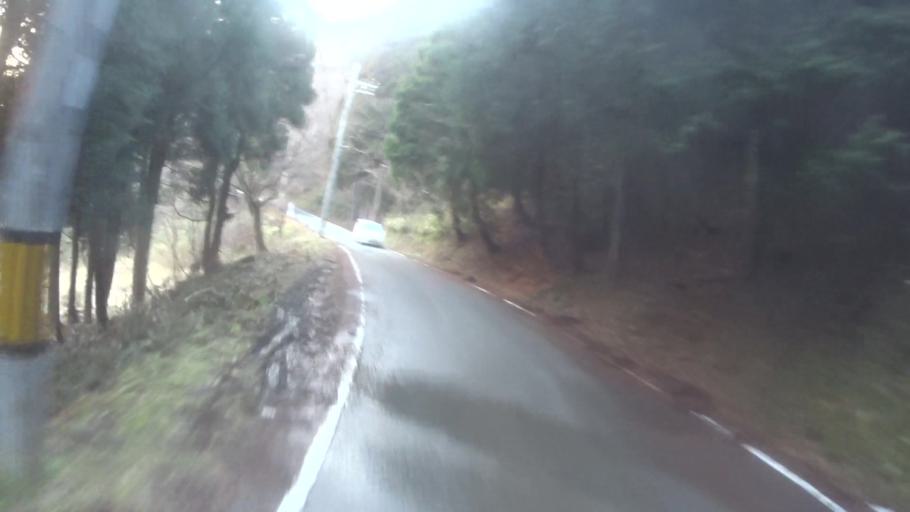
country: JP
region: Kyoto
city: Maizuru
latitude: 35.3865
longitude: 135.4715
